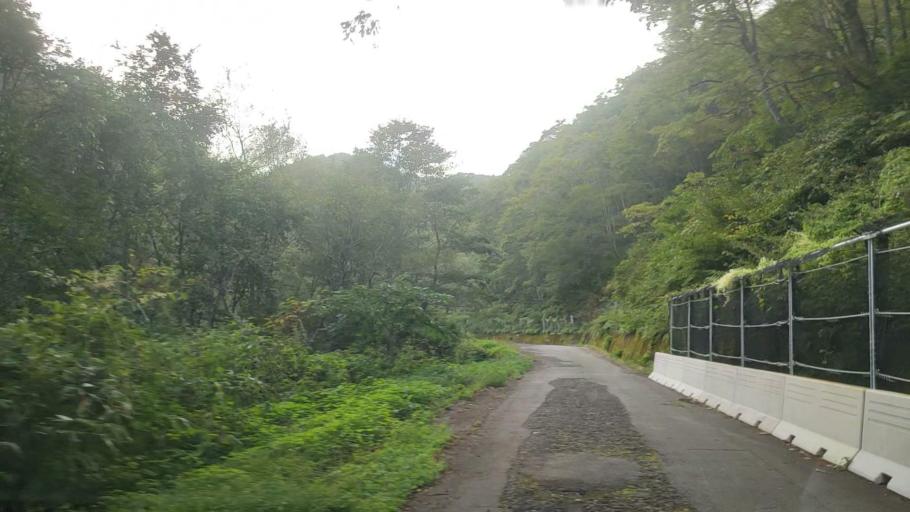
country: JP
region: Toyama
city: Yatsuomachi-higashikumisaka
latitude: 36.3414
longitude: 137.0747
